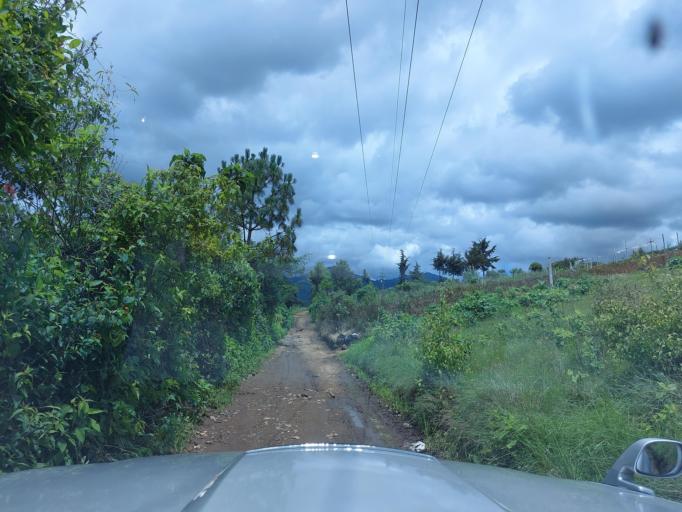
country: GT
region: Chimaltenango
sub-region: Municipio de Chimaltenango
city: Chimaltenango
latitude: 14.6402
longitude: -90.8299
